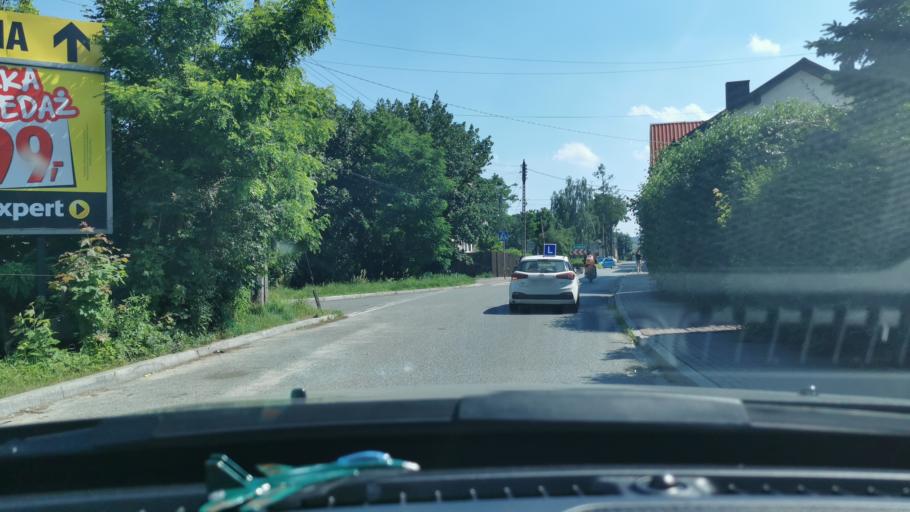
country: PL
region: Lesser Poland Voivodeship
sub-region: Powiat chrzanowski
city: Chrzanow
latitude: 50.1383
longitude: 19.3971
